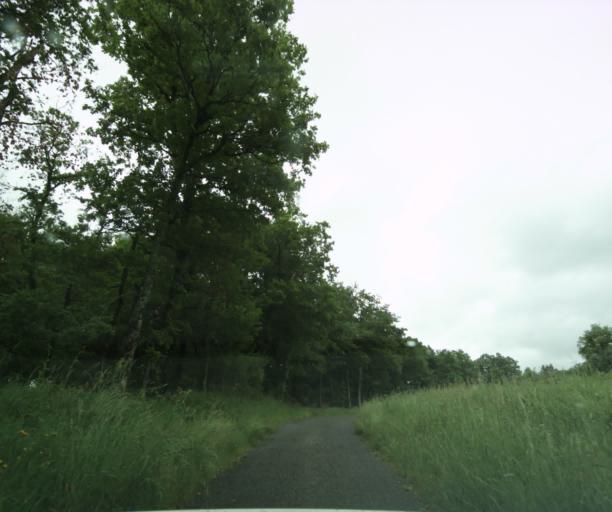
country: FR
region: Bourgogne
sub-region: Departement de Saone-et-Loire
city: Matour
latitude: 46.4401
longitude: 4.4310
